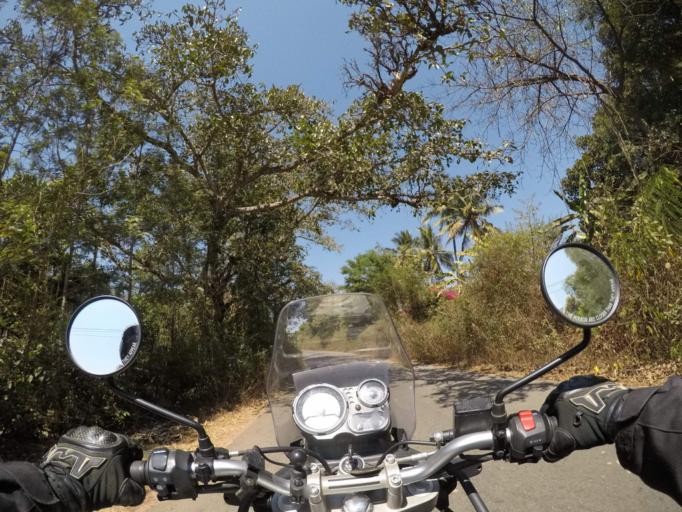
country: IN
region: Karnataka
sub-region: Chikmagalur
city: Mudigere
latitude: 13.0767
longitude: 75.6822
